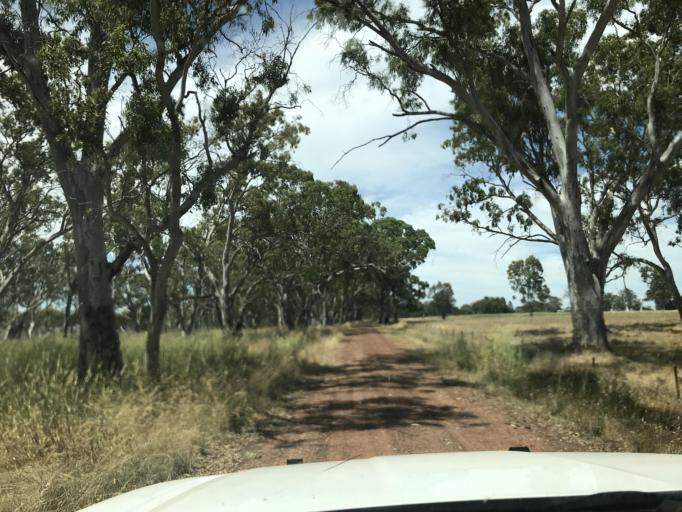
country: AU
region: Victoria
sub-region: Horsham
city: Horsham
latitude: -36.9929
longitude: 141.4967
